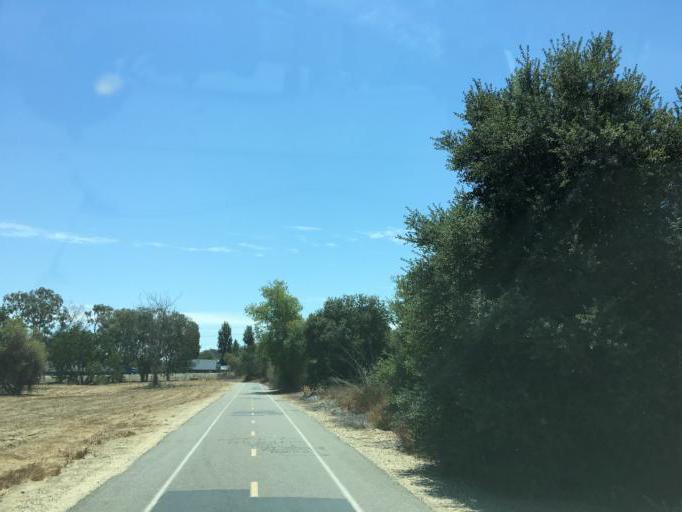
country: US
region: California
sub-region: Los Angeles County
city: South El Monte
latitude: 34.0429
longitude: -118.0717
